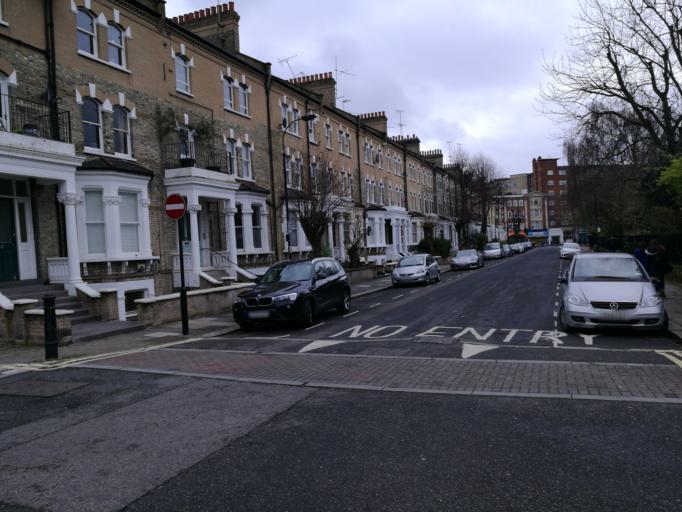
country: GB
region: England
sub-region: Greater London
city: Hammersmith
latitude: 51.4916
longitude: -0.2093
